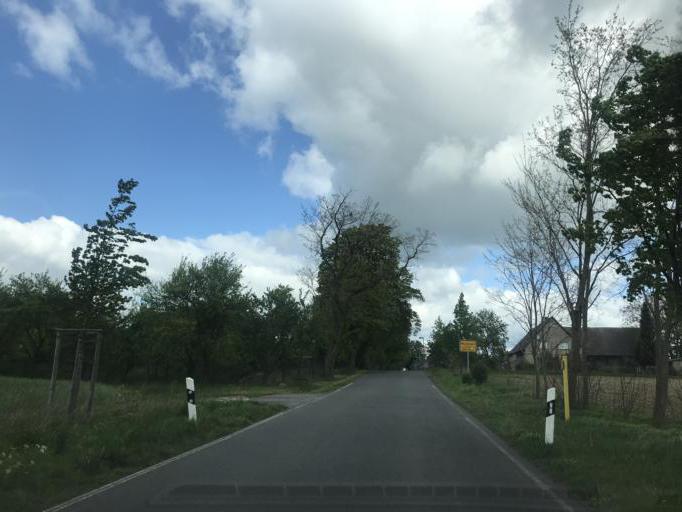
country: DE
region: Brandenburg
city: Gransee
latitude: 52.9197
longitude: 13.1849
